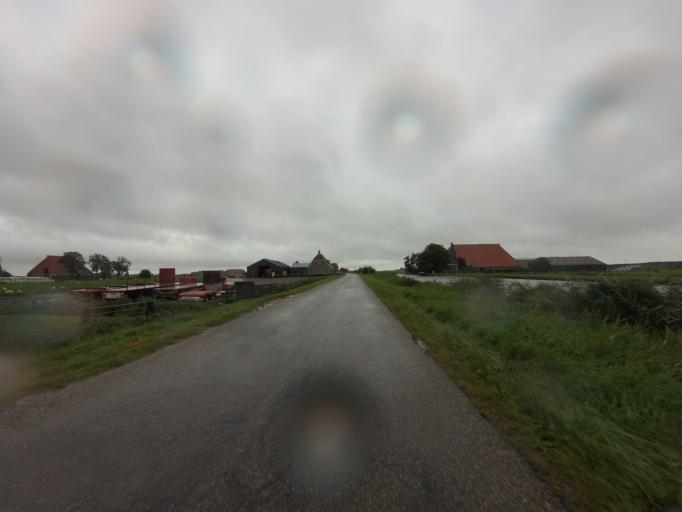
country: NL
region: Friesland
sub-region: Sudwest Fryslan
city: Workum
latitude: 52.9965
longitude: 5.4747
